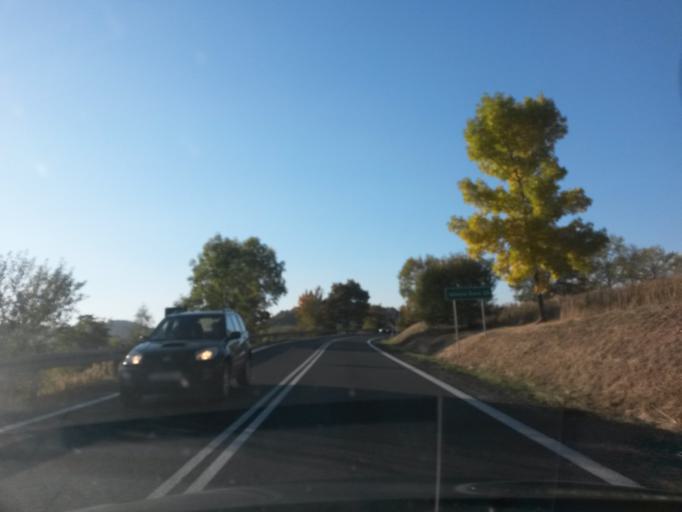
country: PL
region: Lower Silesian Voivodeship
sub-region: Powiat jaworski
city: Bolkow
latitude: 50.9364
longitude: 16.0708
